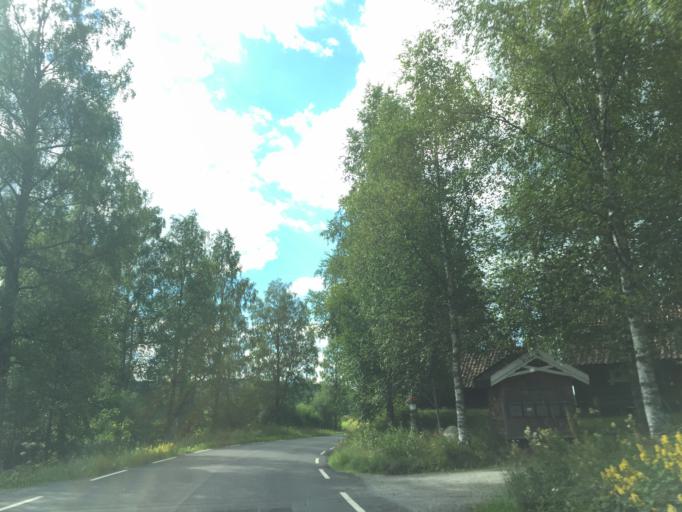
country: NO
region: Hedmark
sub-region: Kongsvinger
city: Spetalen
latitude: 60.1915
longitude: 11.8539
